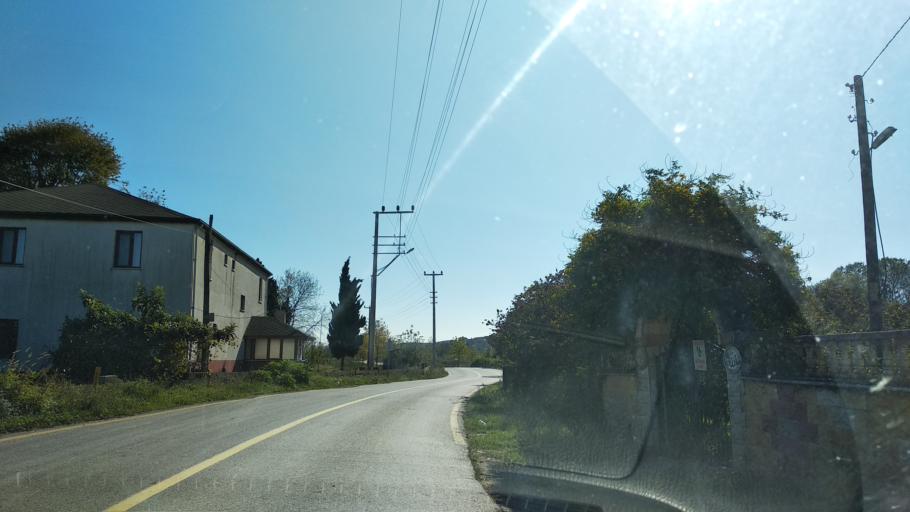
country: TR
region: Sakarya
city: Karasu
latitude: 41.1148
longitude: 30.6440
